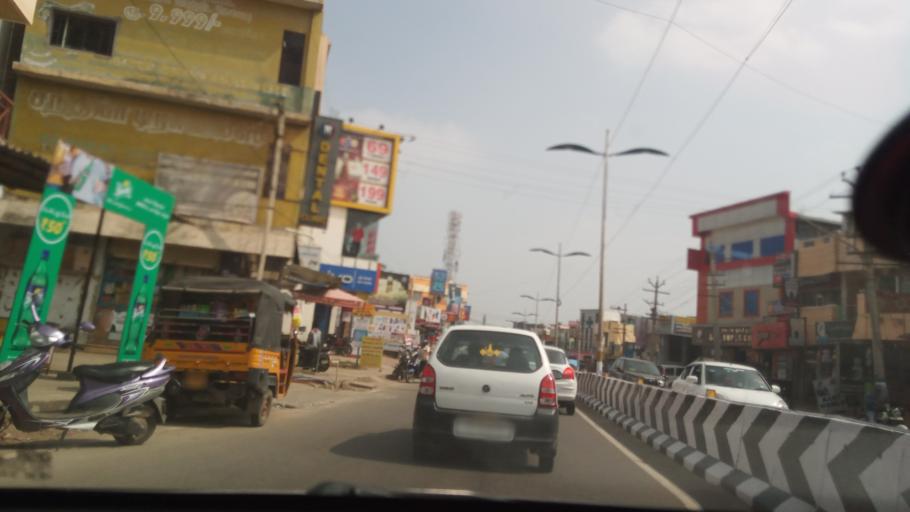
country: IN
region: Tamil Nadu
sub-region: Coimbatore
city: Perur
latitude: 11.0196
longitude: 76.9193
